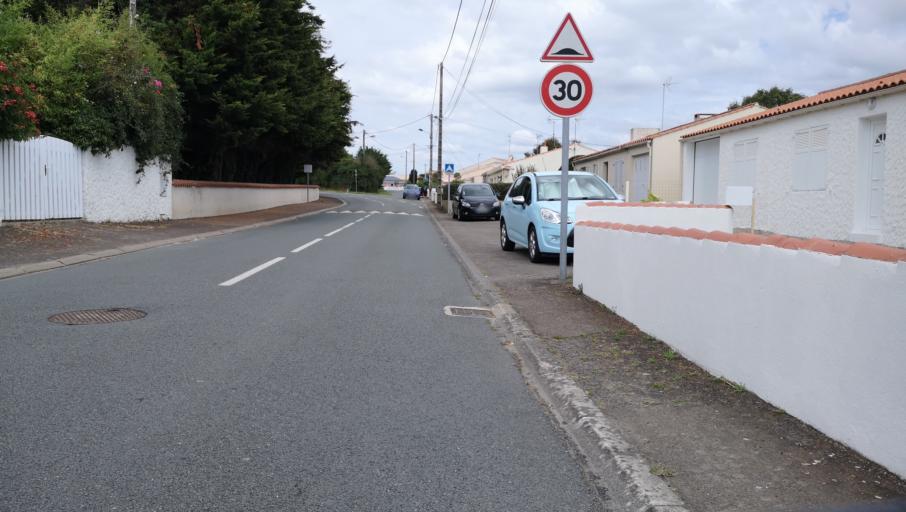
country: FR
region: Pays de la Loire
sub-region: Departement de la Vendee
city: Les Sables-d'Olonne
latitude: 46.5049
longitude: -1.7668
